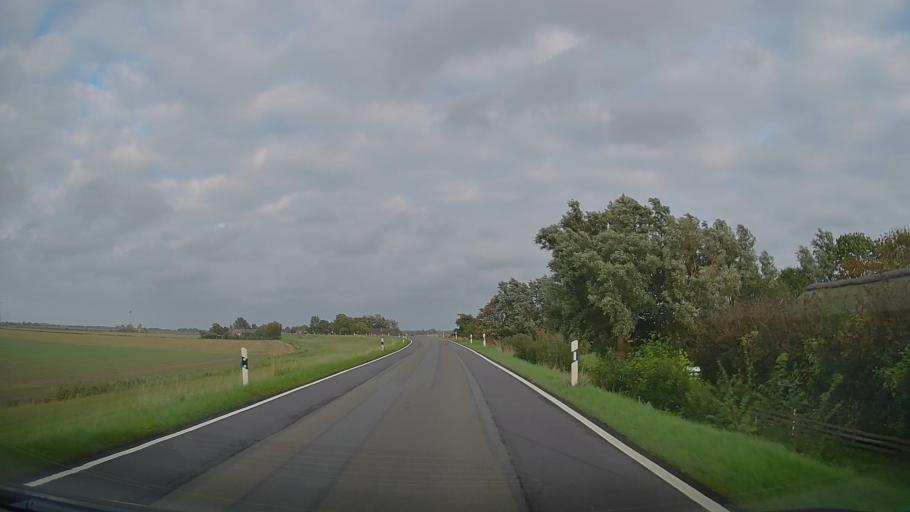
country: DE
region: Schleswig-Holstein
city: Simonsberg
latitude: 54.4329
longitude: 8.9810
